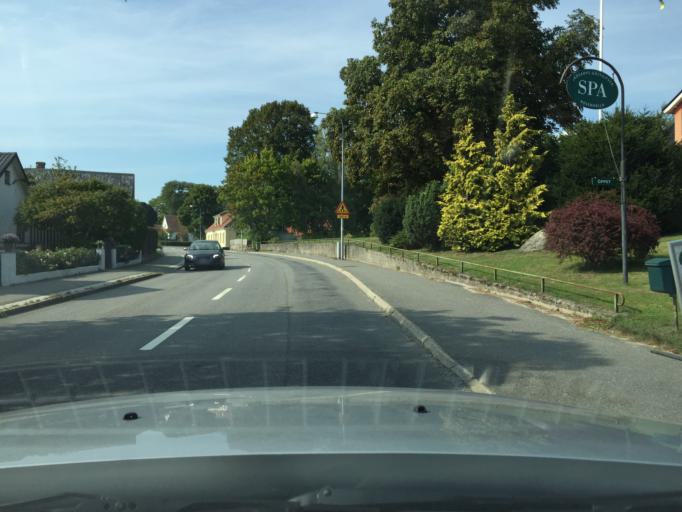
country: SE
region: Skane
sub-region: Kristianstads Kommun
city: Degeberga
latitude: 55.7254
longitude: 14.1027
